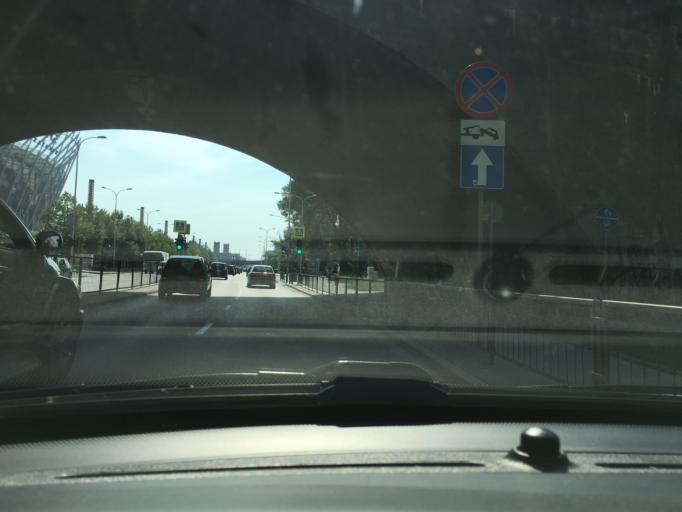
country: PL
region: Masovian Voivodeship
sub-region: Warszawa
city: Praga Polnoc
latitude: 52.2407
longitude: 21.0406
